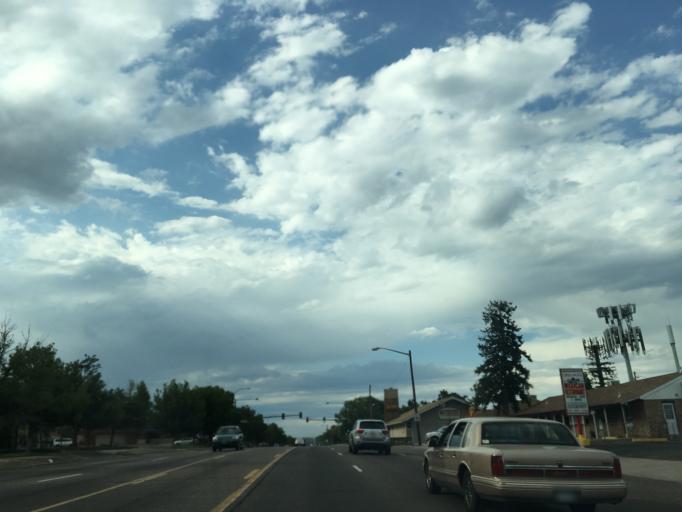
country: US
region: Colorado
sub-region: Jefferson County
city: Lakewood
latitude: 39.7120
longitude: -105.0532
